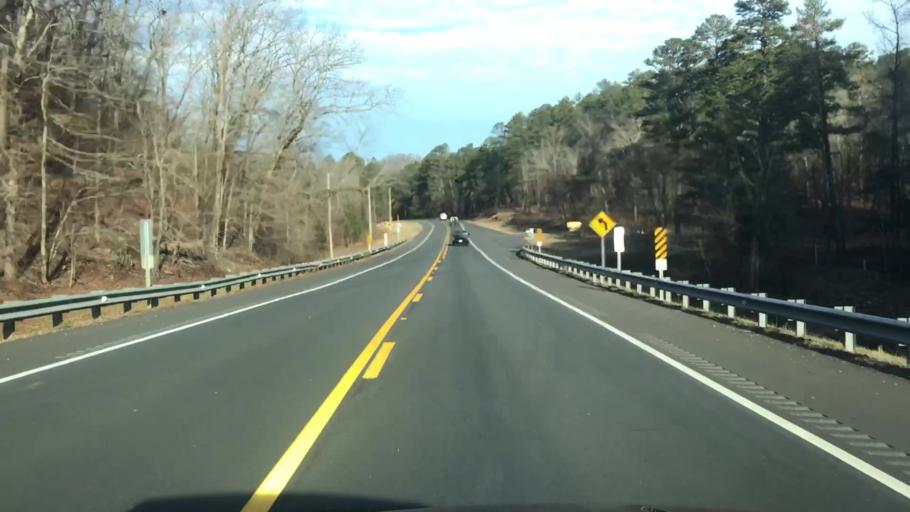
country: US
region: Arkansas
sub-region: Pike County
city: Glenwood
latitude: 34.5149
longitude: -93.3831
